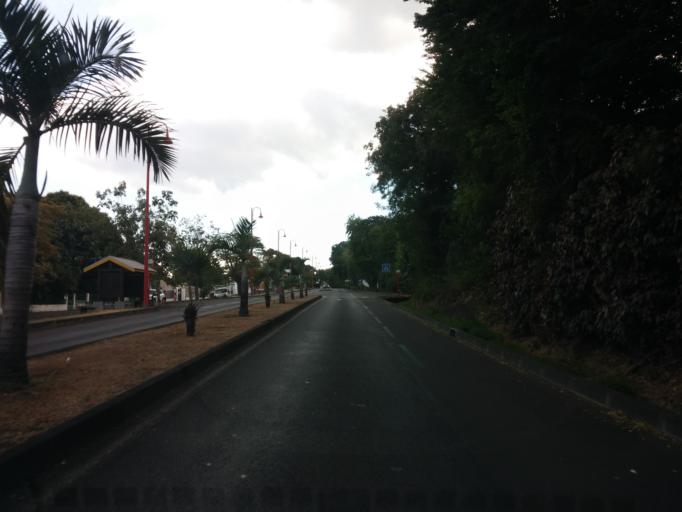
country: RE
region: Reunion
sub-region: Reunion
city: La Possession
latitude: -20.9369
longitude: 55.3328
